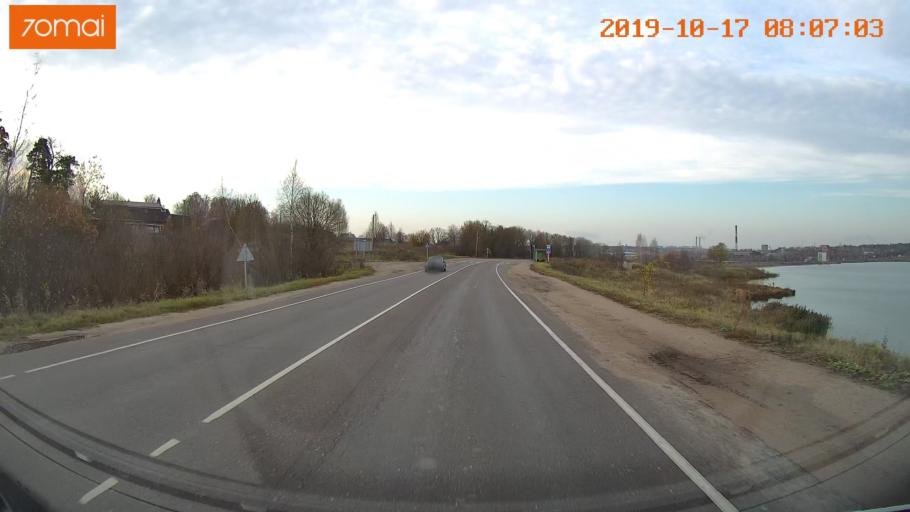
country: RU
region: Vladimir
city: Kol'chugino
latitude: 56.3183
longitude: 39.4026
